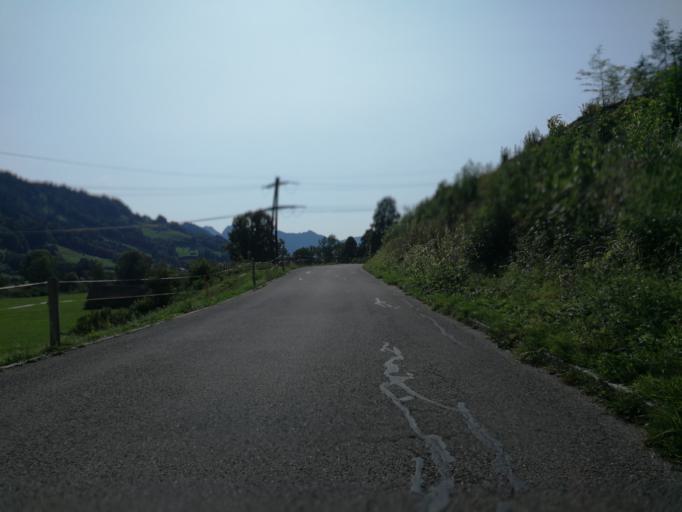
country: CH
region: Saint Gallen
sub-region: Wahlkreis Toggenburg
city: Wattwil
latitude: 47.2784
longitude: 9.0976
